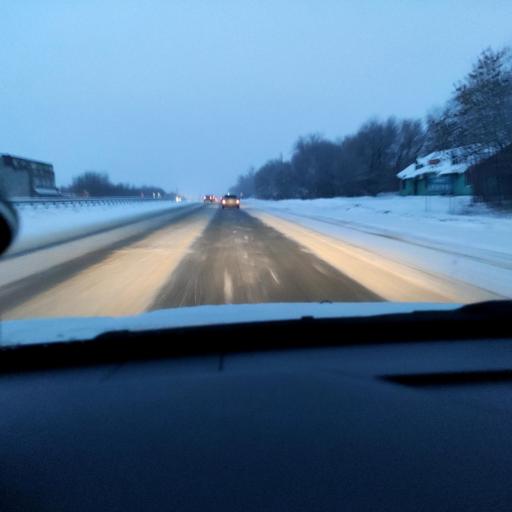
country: RU
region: Samara
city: Smyshlyayevka
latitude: 53.2591
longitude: 50.4504
